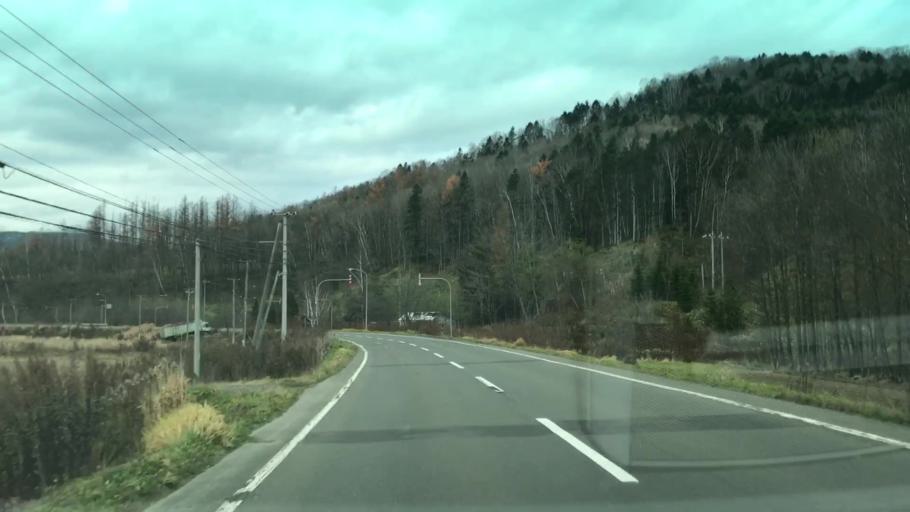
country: JP
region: Hokkaido
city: Shimo-furano
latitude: 42.9740
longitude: 142.4198
